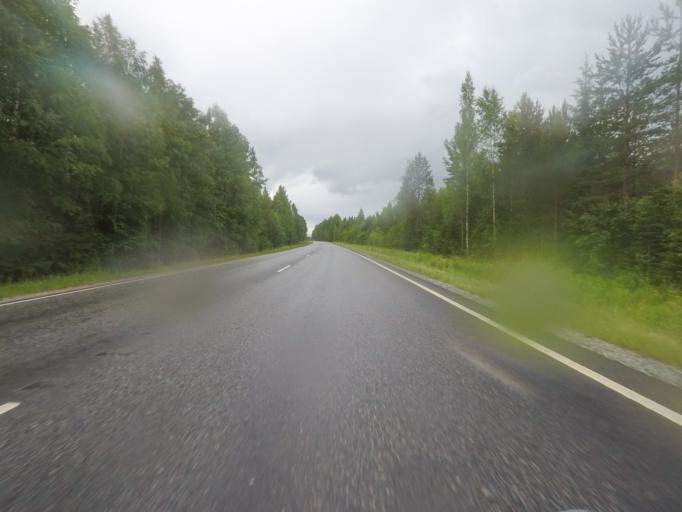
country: FI
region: Central Finland
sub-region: Jyvaeskylae
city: Toivakka
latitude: 62.2221
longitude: 26.2022
